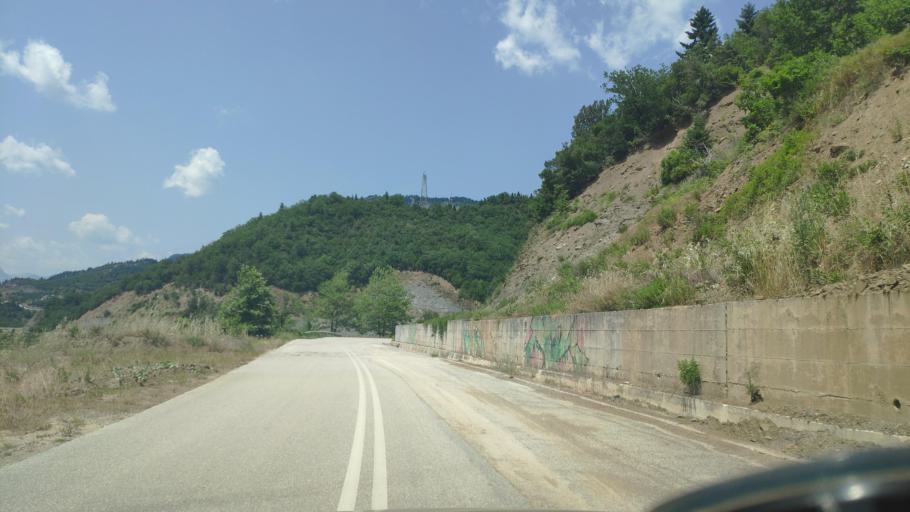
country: GR
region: Epirus
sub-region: Nomos Artas
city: Ano Kalentini
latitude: 39.2720
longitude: 21.3301
